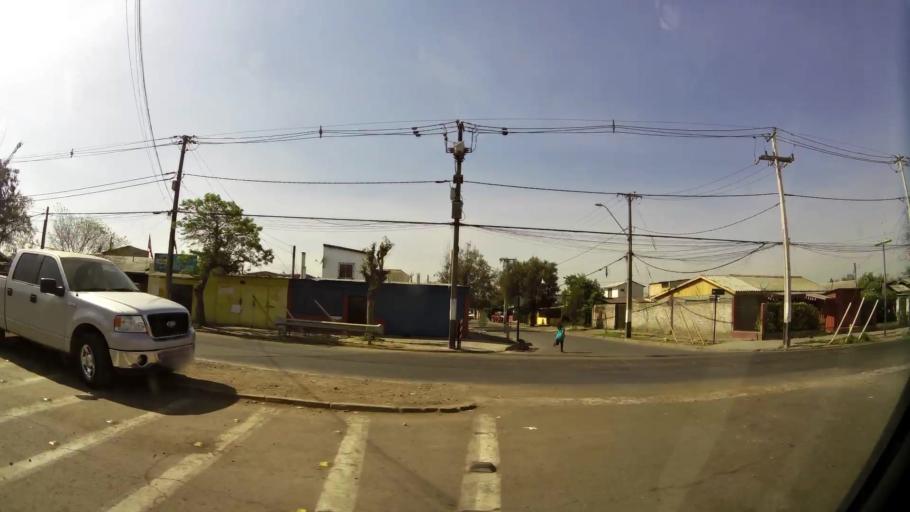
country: CL
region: Santiago Metropolitan
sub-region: Provincia de Santiago
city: Lo Prado
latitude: -33.4317
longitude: -70.7479
